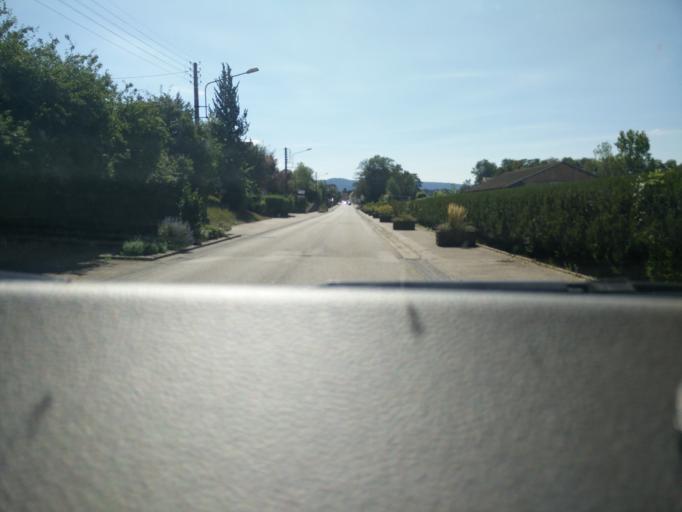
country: FR
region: Lorraine
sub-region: Departement des Vosges
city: Etival-Clairefontaine
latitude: 48.3688
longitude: 6.8776
